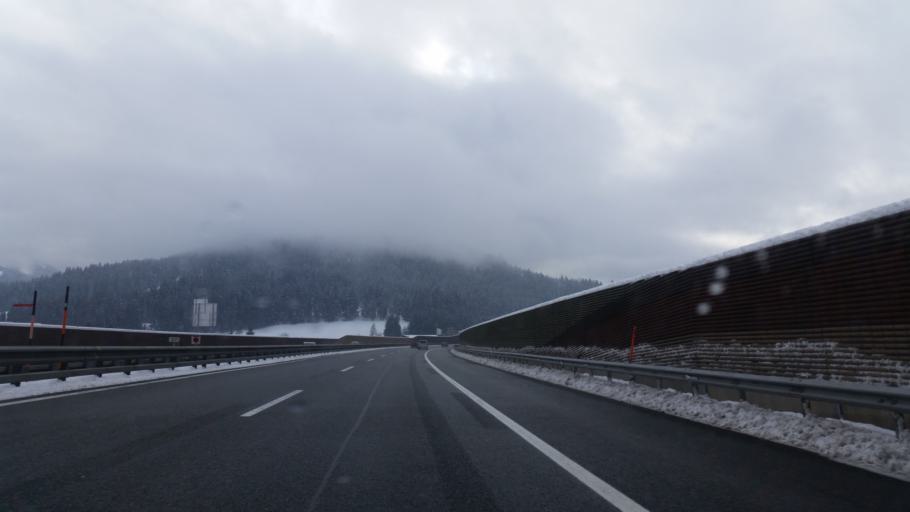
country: AT
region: Salzburg
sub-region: Politischer Bezirk Sankt Johann im Pongau
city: Eben im Pongau
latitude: 47.3859
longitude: 13.4012
